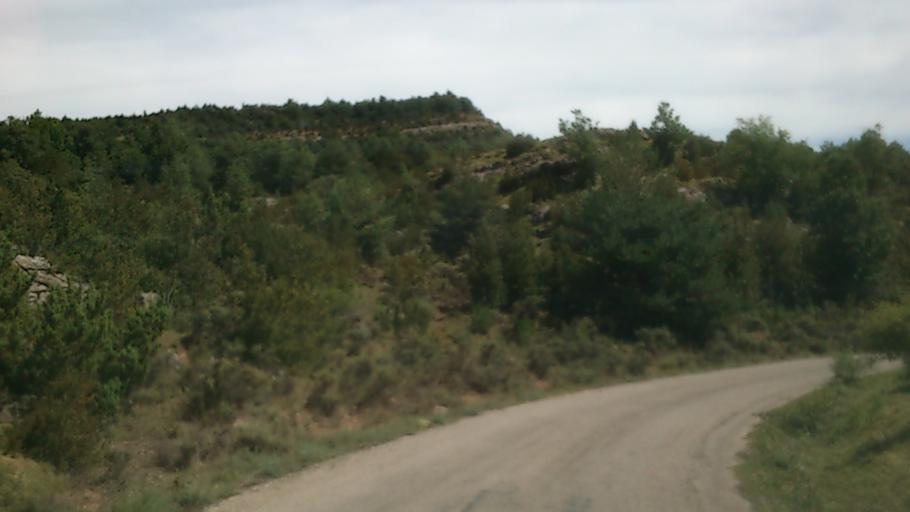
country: ES
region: Aragon
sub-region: Provincia de Huesca
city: Arguis
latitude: 42.3180
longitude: -0.2816
